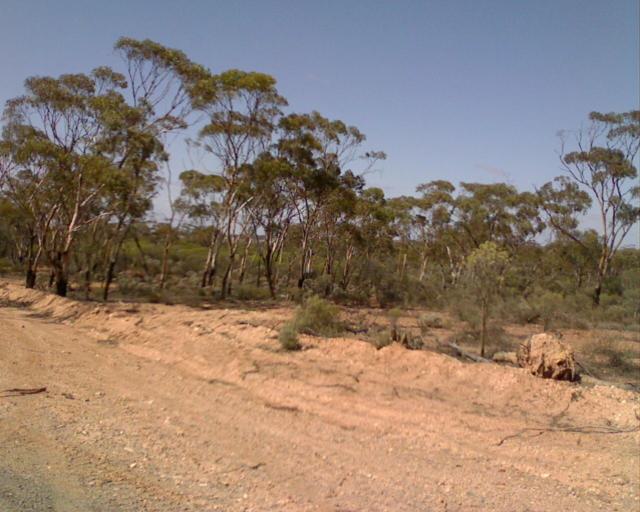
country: AU
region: Western Australia
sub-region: Kalgoorlie/Boulder
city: Boulder
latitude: -30.8349
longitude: 121.3830
